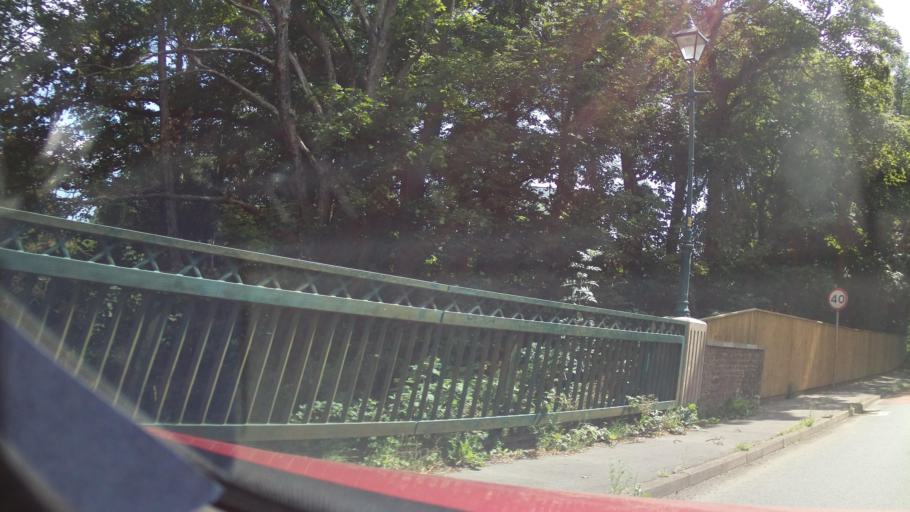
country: GB
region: England
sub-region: Wiltshire
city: Malmesbury
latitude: 51.5755
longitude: -2.0832
